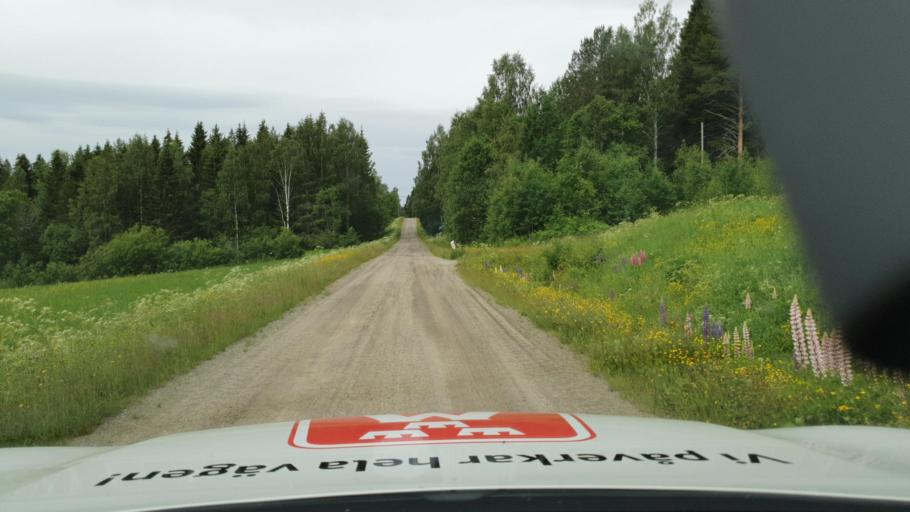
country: SE
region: Vaesterbotten
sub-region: Robertsfors Kommun
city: Robertsfors
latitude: 64.2833
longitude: 20.6742
